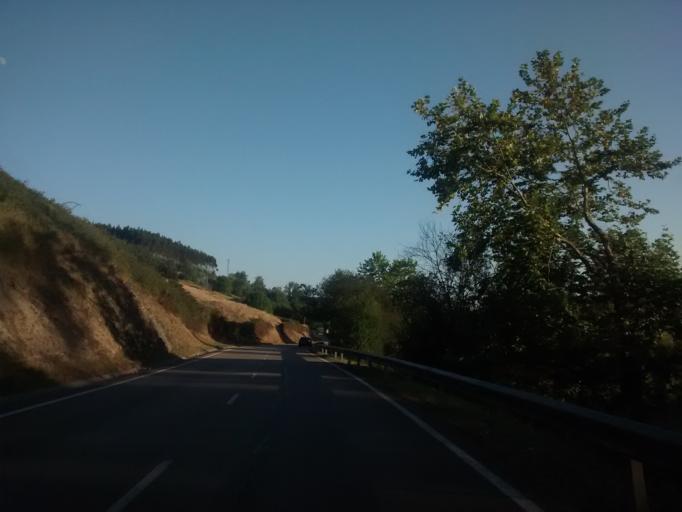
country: ES
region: Cantabria
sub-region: Provincia de Cantabria
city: San Miguel de Meruelo
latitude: 43.4682
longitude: -3.5862
